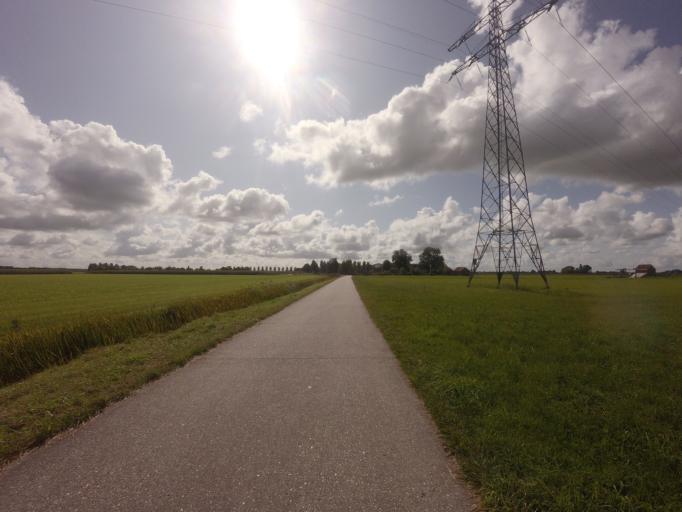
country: NL
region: Friesland
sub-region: Sudwest Fryslan
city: Sneek
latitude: 53.0631
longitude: 5.6332
